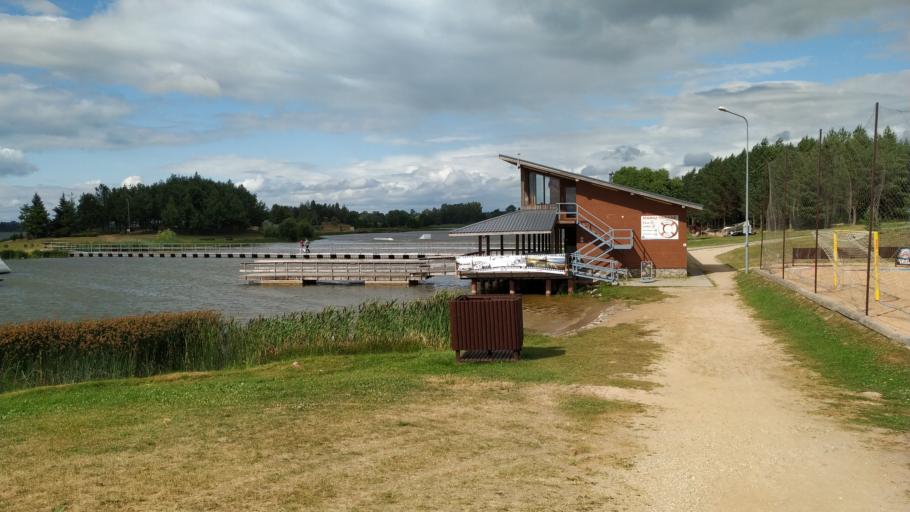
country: LT
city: Kupiskis
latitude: 55.8505
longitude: 24.9767
